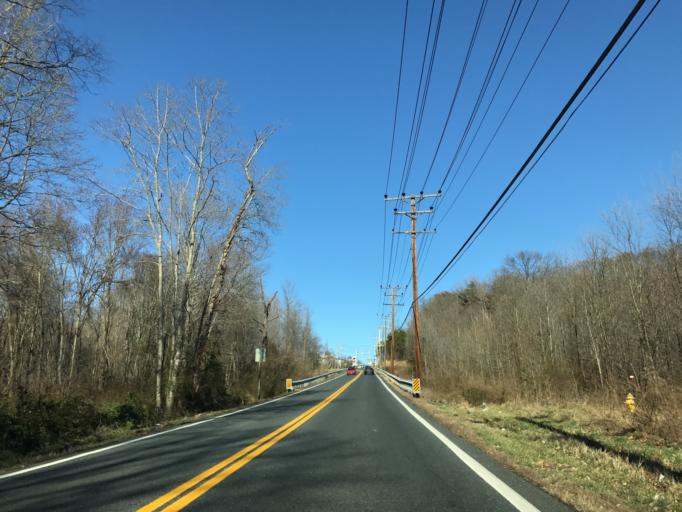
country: US
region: Maryland
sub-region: Harford County
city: Riverside
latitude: 39.4778
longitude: -76.2586
